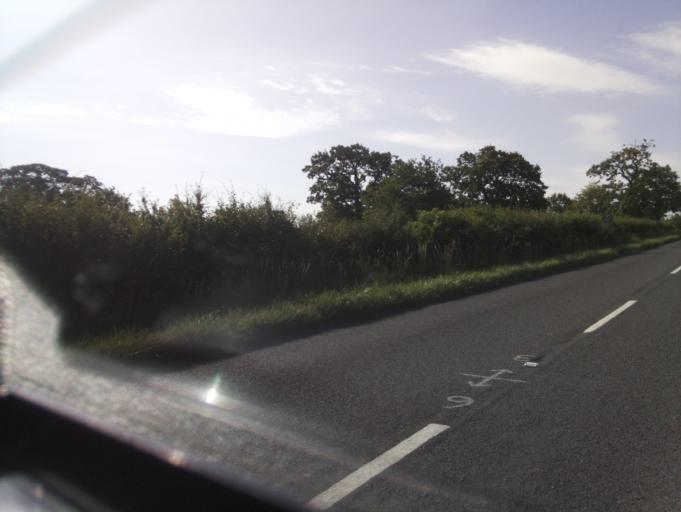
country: GB
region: England
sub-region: Oxfordshire
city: Faringdon
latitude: 51.6852
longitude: -1.5896
